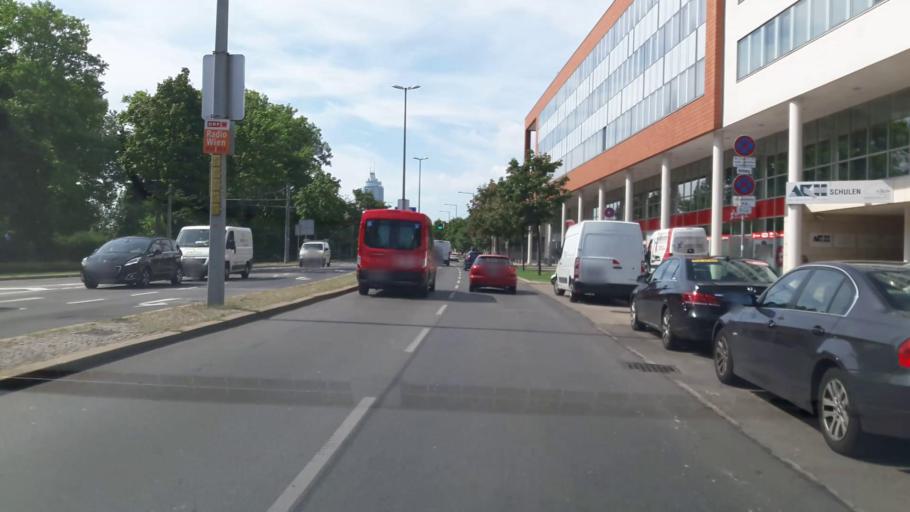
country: AT
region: Vienna
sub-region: Wien Stadt
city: Vienna
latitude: 48.2535
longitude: 16.3937
